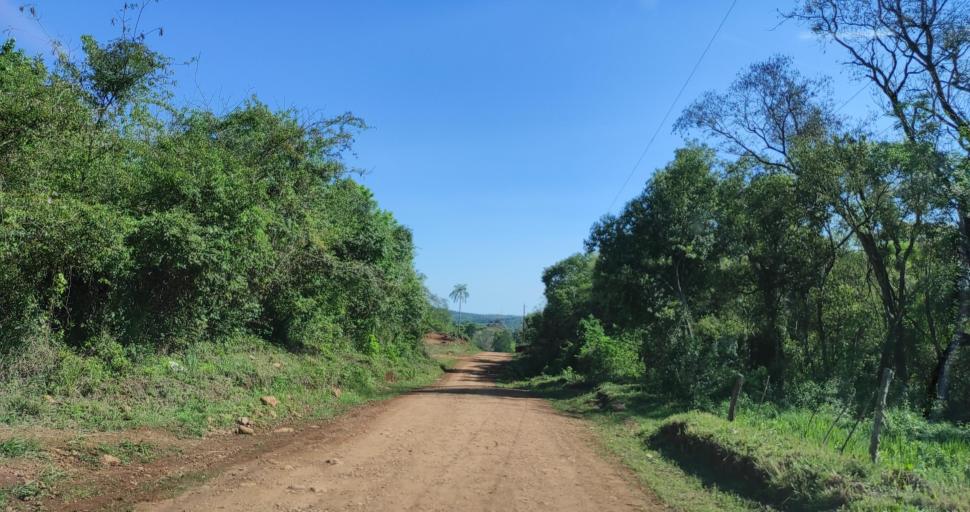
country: AR
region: Misiones
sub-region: Departamento de Candelaria
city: Loreto
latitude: -27.3156
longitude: -55.5351
